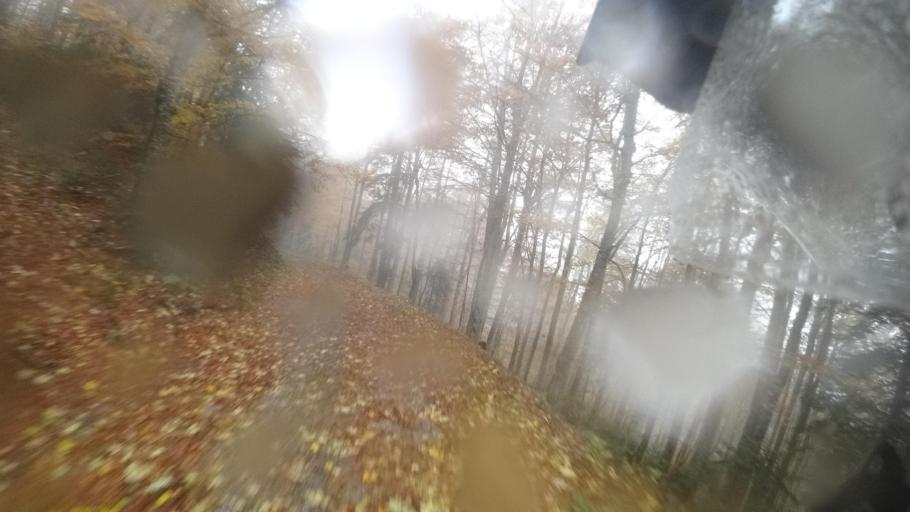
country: HR
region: Primorsko-Goranska
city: Vrbovsko
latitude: 45.2955
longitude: 14.9385
